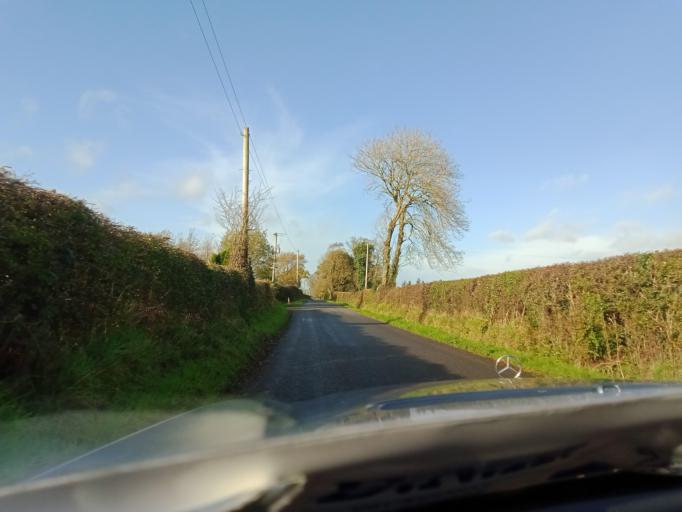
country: IE
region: Leinster
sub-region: Kilkenny
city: Mooncoin
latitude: 52.3307
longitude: -7.2555
